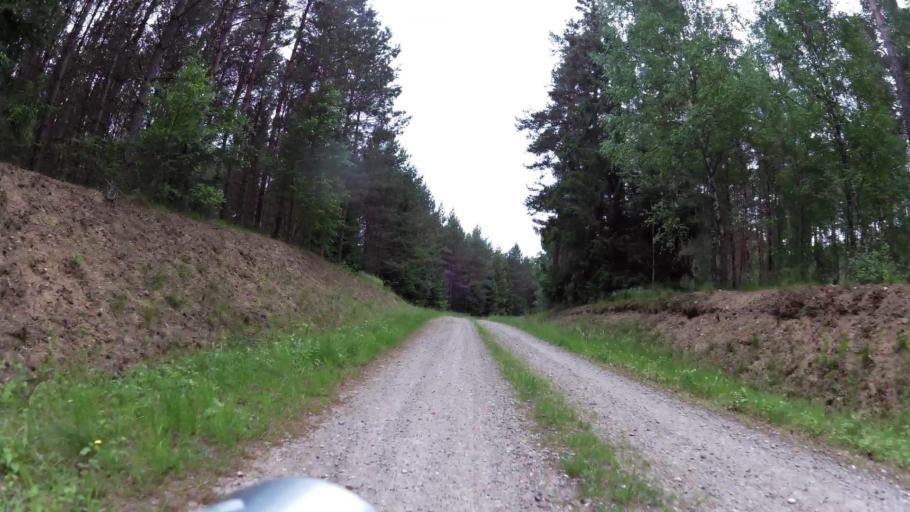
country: PL
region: West Pomeranian Voivodeship
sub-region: Powiat szczecinecki
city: Bialy Bor
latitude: 53.9409
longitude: 16.8308
